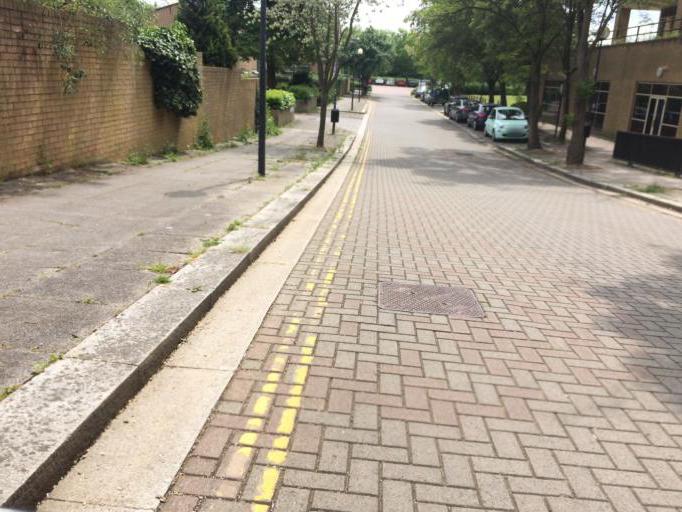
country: GB
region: England
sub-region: Milton Keynes
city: Milton Keynes
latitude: 52.0392
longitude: -0.7553
